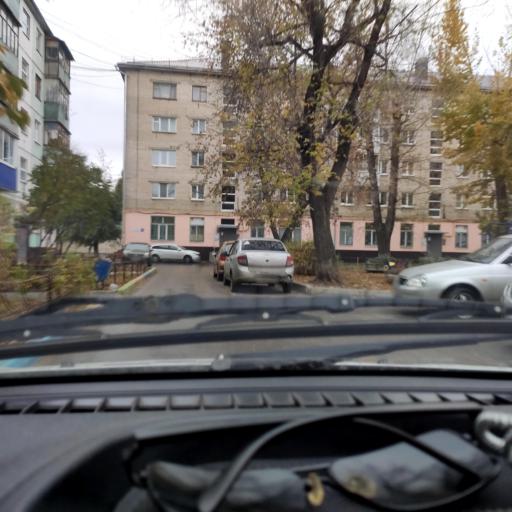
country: RU
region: Samara
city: Tol'yatti
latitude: 53.5135
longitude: 49.4286
